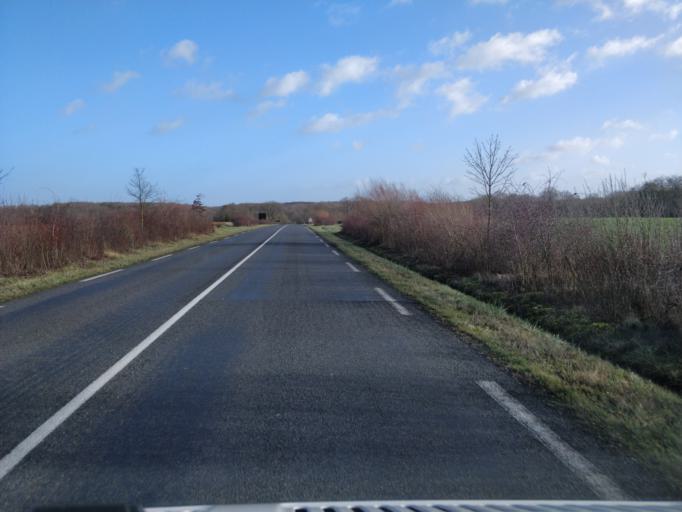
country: FR
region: Ile-de-France
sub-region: Departement de Seine-et-Marne
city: Lorrez-le-Bocage-Preaux
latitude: 48.2191
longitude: 2.8972
